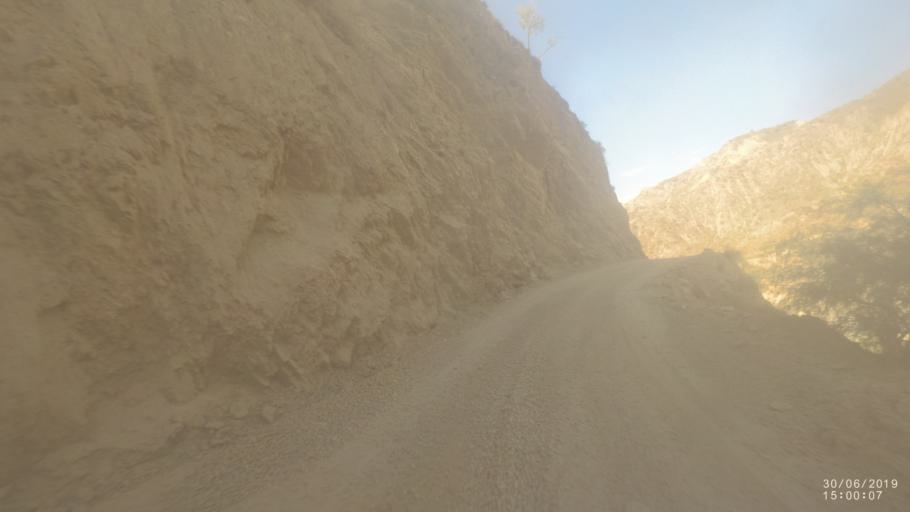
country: BO
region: Cochabamba
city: Irpa Irpa
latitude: -17.7365
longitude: -66.3422
